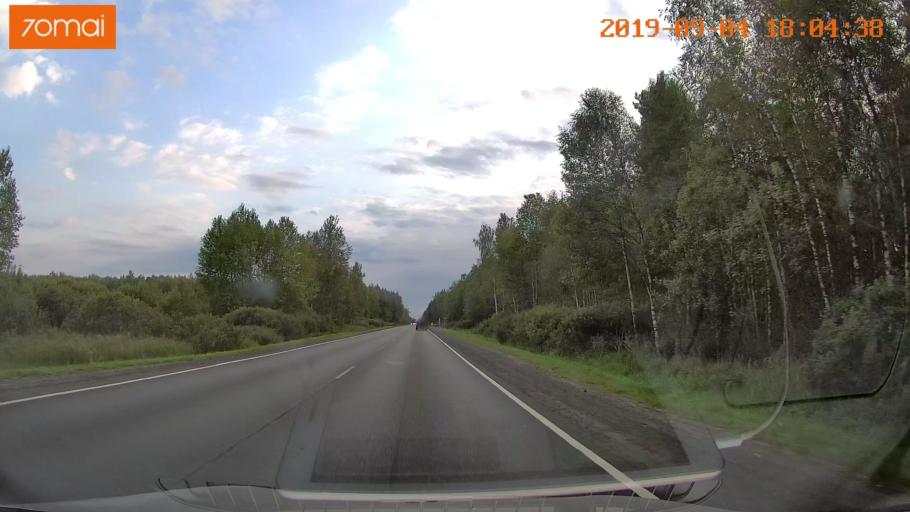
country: RU
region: Moskovskaya
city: Il'inskiy Pogost
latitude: 55.4501
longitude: 38.8366
